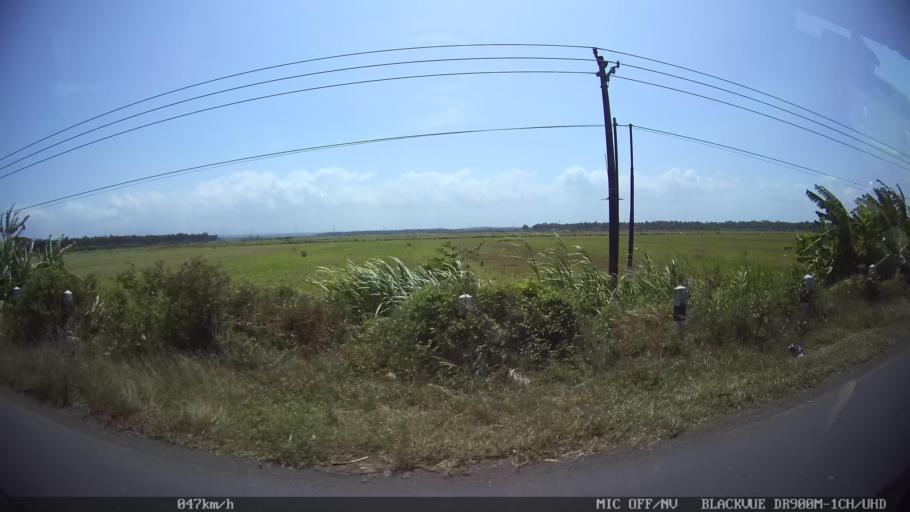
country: ID
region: Daerah Istimewa Yogyakarta
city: Srandakan
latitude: -7.9457
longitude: 110.1757
